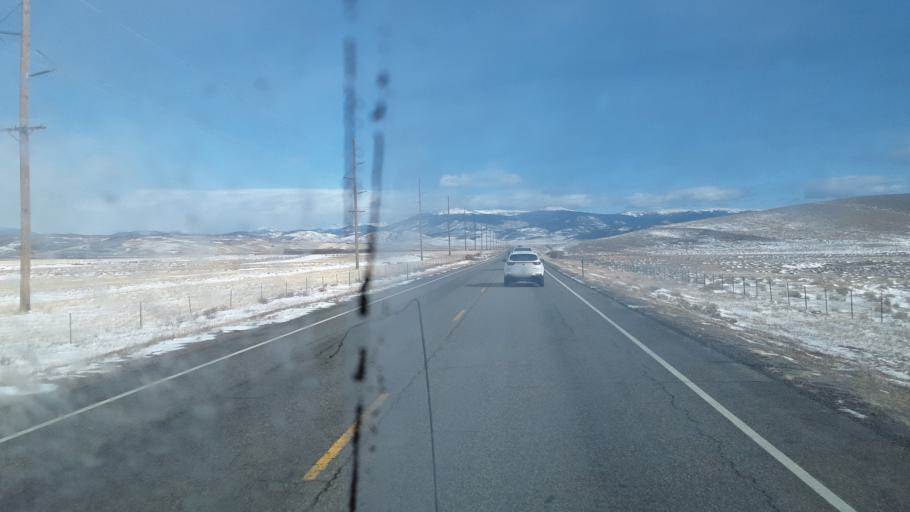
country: US
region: Colorado
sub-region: Park County
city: Fairplay
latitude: 39.3351
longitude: -105.8634
